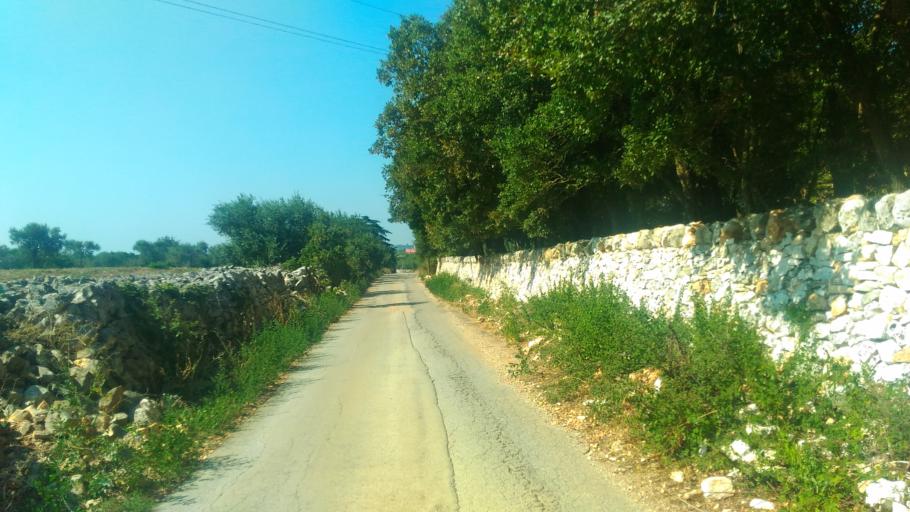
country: IT
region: Apulia
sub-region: Provincia di Bari
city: Noci
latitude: 40.8176
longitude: 17.1771
